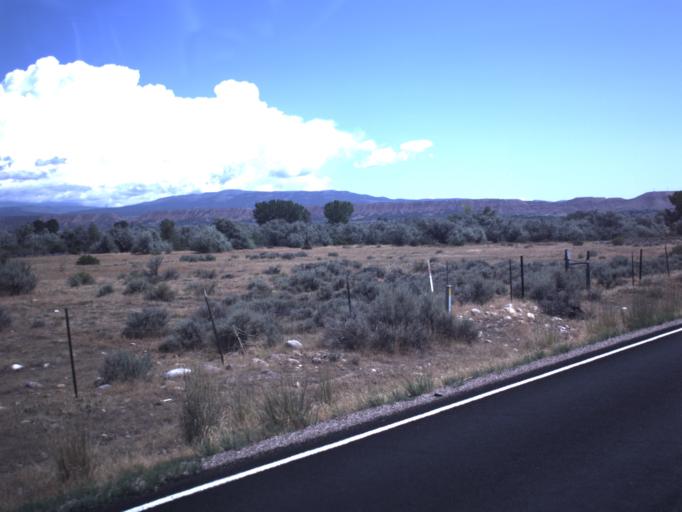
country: US
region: Utah
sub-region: Duchesne County
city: Roosevelt
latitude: 40.4037
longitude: -109.8679
